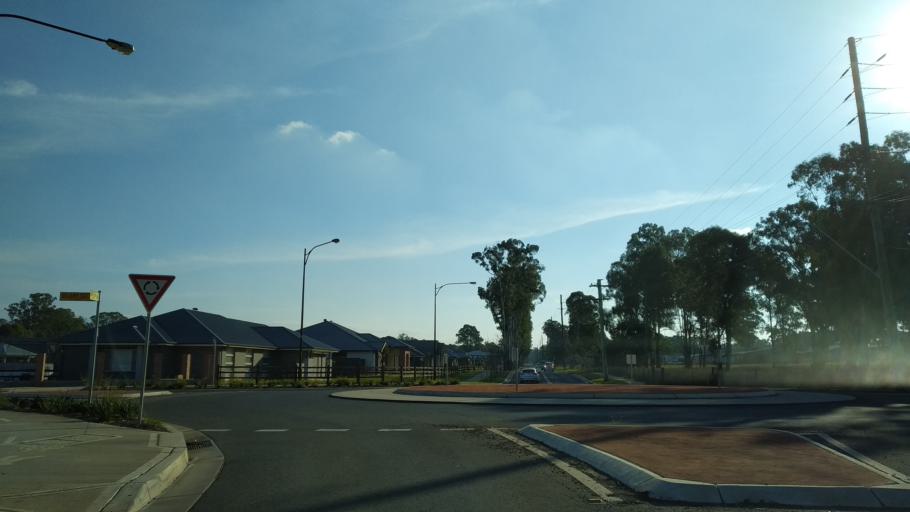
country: AU
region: New South Wales
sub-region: Penrith Municipality
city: Werrington Downs
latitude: -33.7145
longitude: 150.7426
